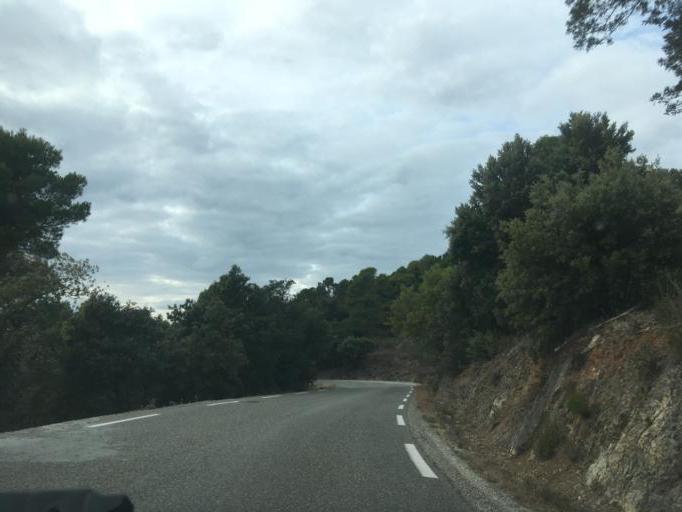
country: FR
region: Provence-Alpes-Cote d'Azur
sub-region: Departement du Var
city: Villecroze
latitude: 43.5853
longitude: 6.3069
